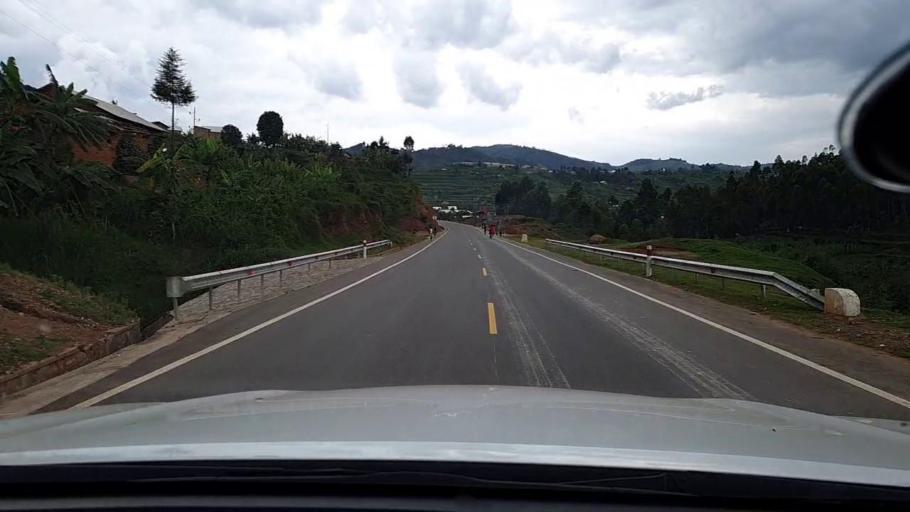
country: RW
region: Northern Province
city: Byumba
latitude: -1.6392
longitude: 29.9267
